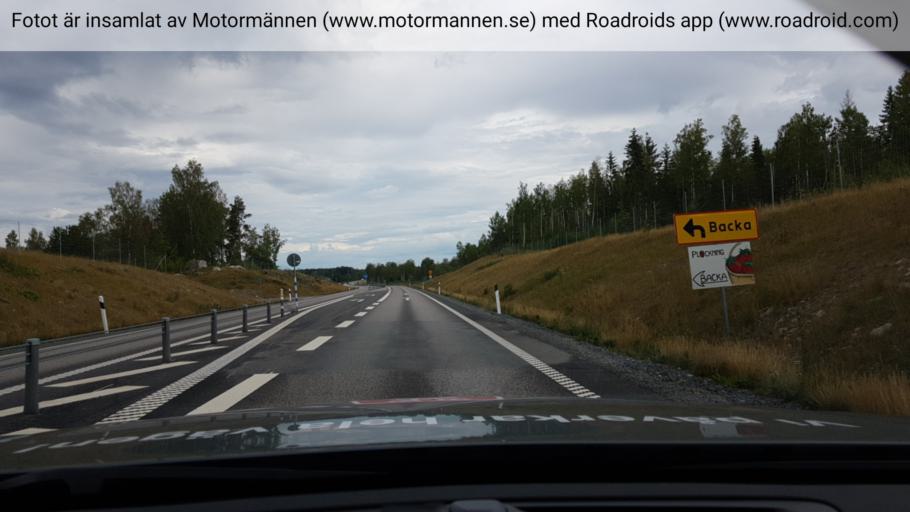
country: SE
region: Uppsala
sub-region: Heby Kommun
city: Heby
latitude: 59.9946
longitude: 16.8532
